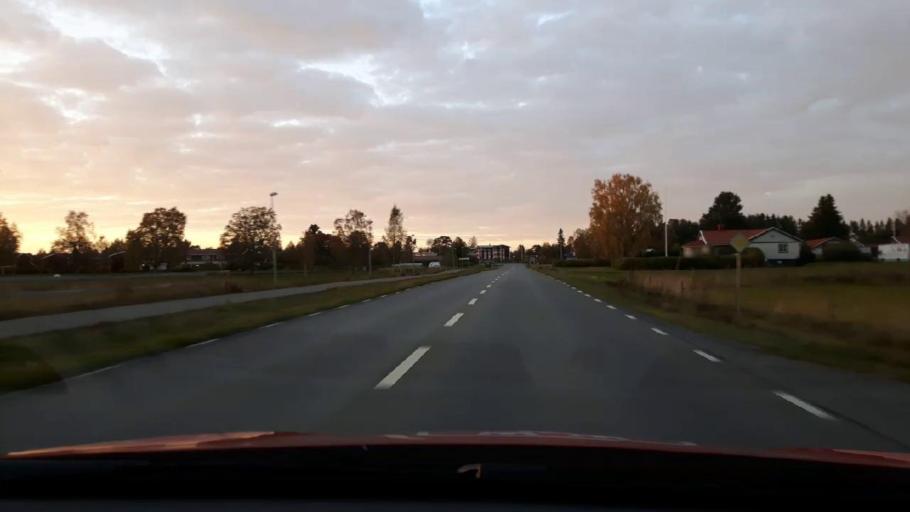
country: SE
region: Jaemtland
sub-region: OEstersunds Kommun
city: Ostersund
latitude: 63.2423
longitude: 14.5734
